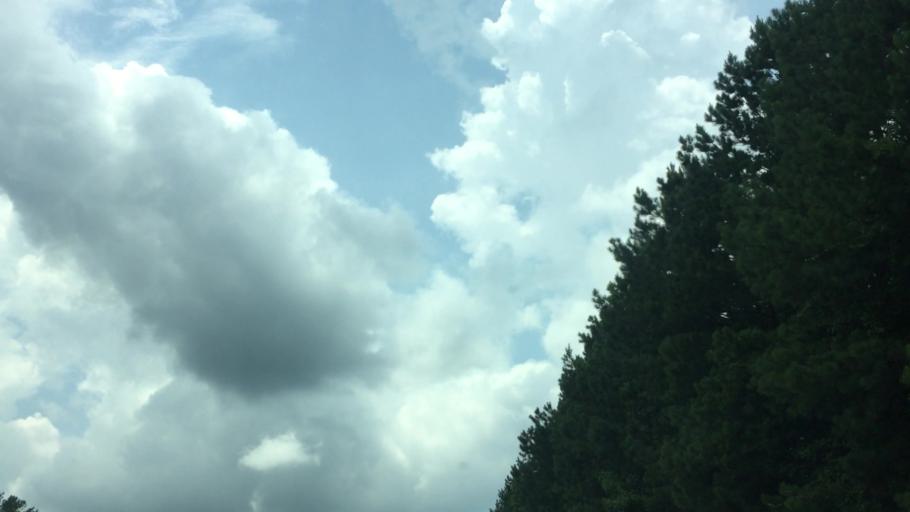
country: US
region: Georgia
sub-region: Fulton County
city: Fairburn
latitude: 33.6167
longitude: -84.5981
